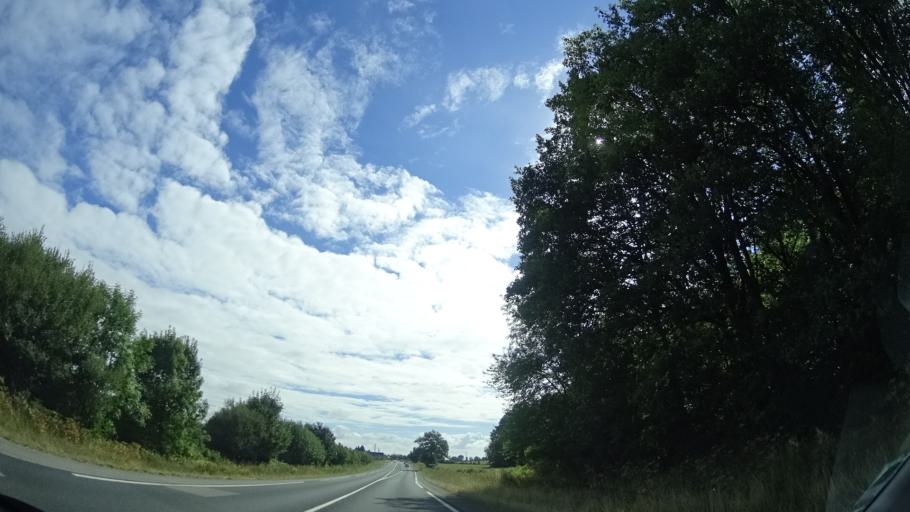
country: FR
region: Pays de la Loire
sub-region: Departement de la Mayenne
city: Port-Brillet
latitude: 48.0754
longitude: -0.9793
